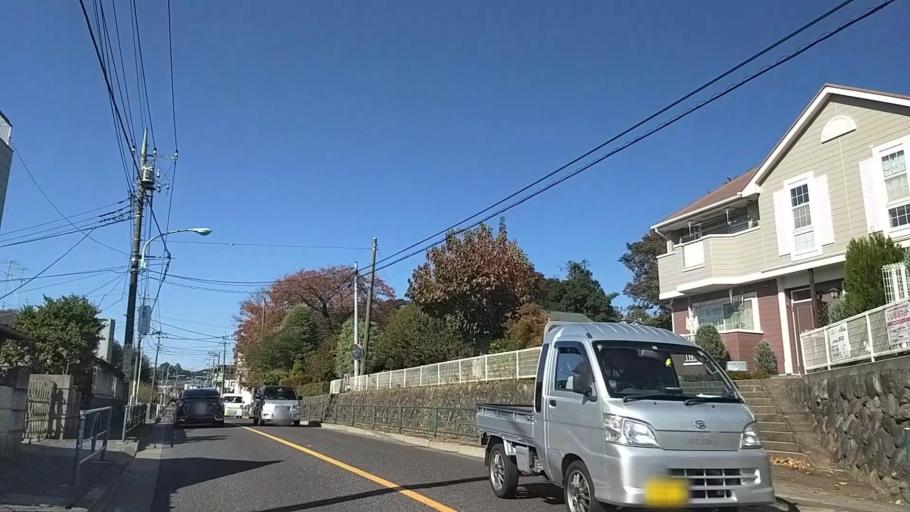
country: JP
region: Tokyo
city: Hachioji
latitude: 35.6053
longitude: 139.3420
